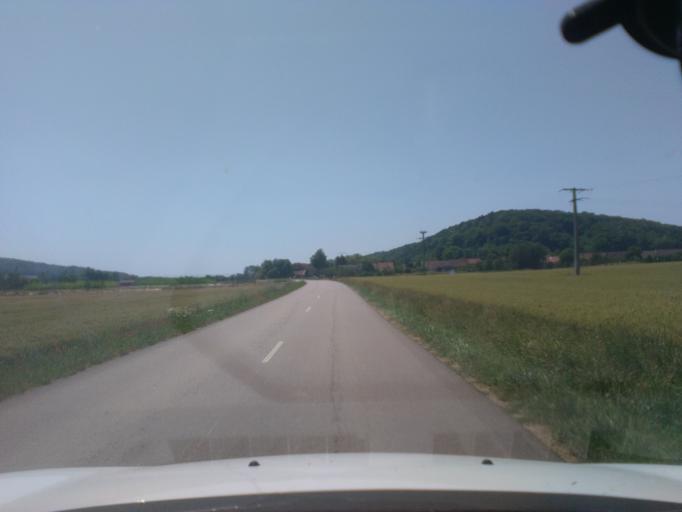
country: FR
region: Lorraine
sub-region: Departement des Vosges
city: Liffol-le-Grand
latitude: 48.3688
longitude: 5.6102
